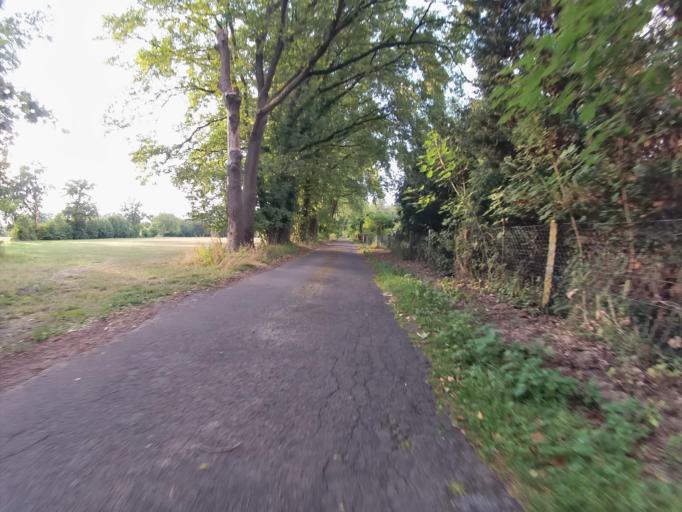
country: DE
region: North Rhine-Westphalia
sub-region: Regierungsbezirk Munster
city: Westerkappeln
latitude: 52.3626
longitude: 7.8955
